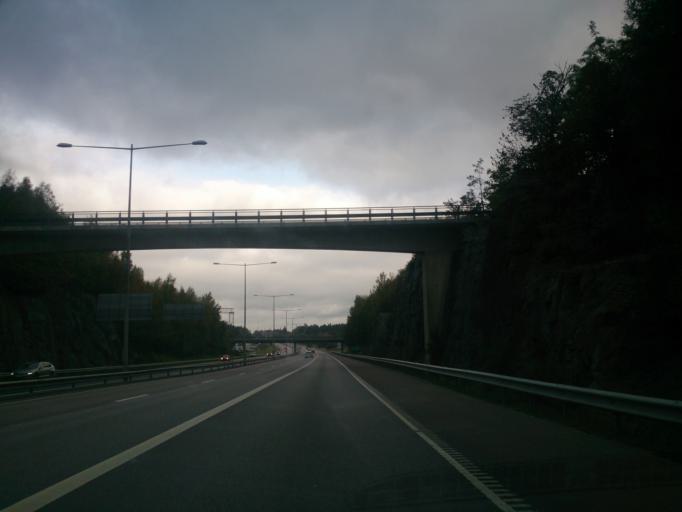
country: SE
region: Stockholm
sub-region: Haninge Kommun
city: Haninge
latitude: 59.1820
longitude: 18.1537
